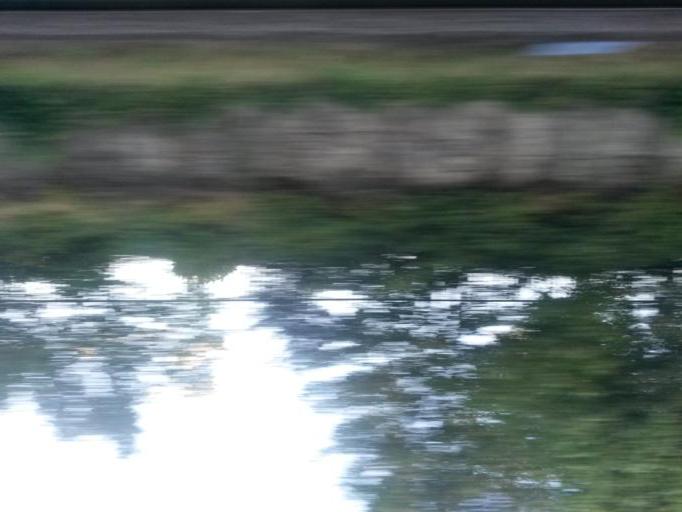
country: GB
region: England
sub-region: Greater London
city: Earlsfield
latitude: 51.4527
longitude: -0.1696
